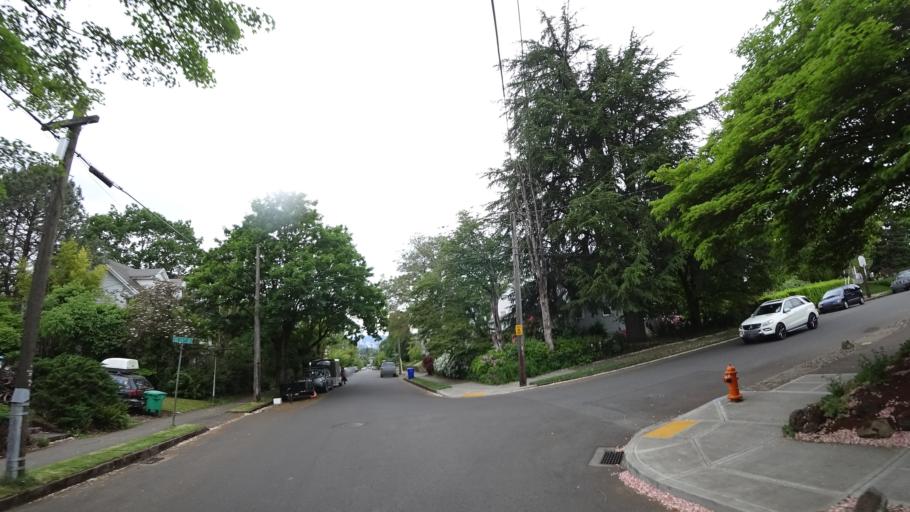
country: US
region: Oregon
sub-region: Multnomah County
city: Lents
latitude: 45.5154
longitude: -122.6077
